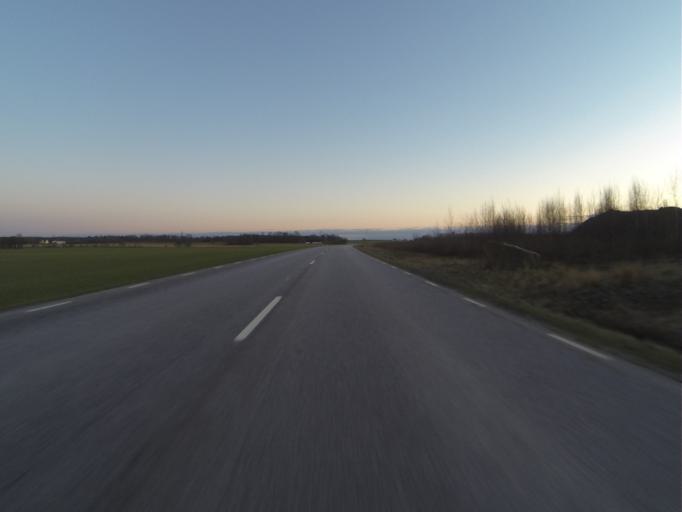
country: SE
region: Skane
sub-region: Lunds Kommun
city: Lund
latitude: 55.7047
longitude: 13.3030
